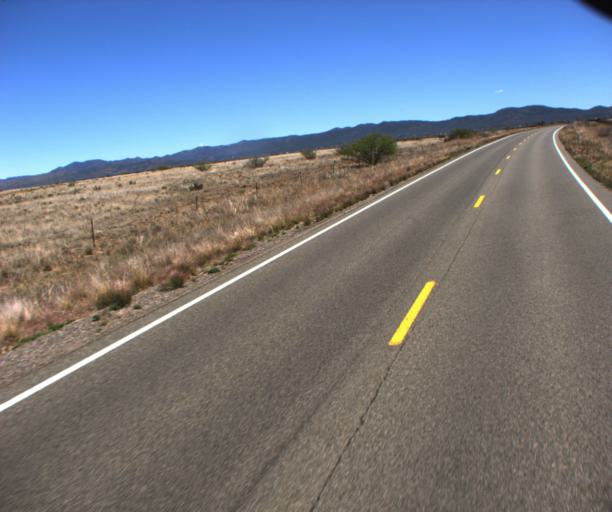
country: US
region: Arizona
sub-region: Yavapai County
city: Prescott
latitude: 34.3871
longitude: -112.6479
